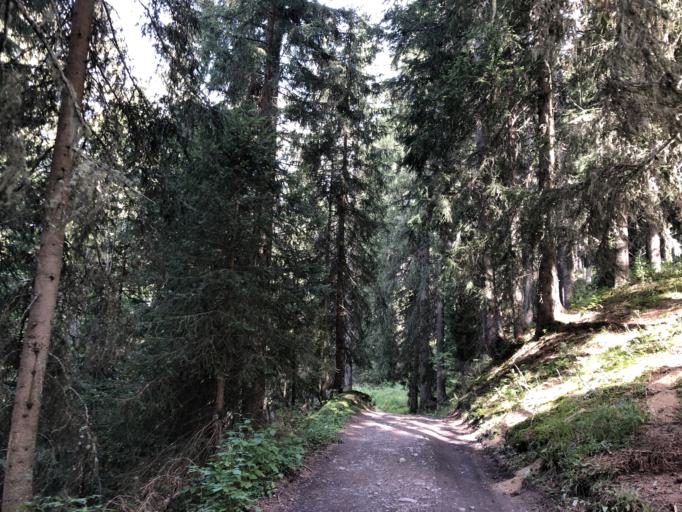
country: FR
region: Rhone-Alpes
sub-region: Departement de la Haute-Savoie
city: Megeve
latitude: 45.8295
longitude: 6.6543
